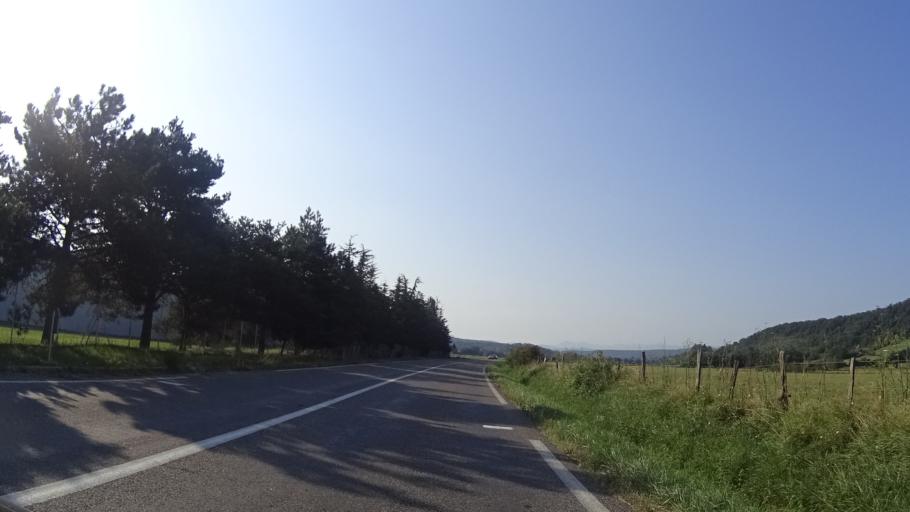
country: FR
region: Midi-Pyrenees
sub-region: Departement de l'Ariege
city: Mirepoix
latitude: 43.0458
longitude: 1.8942
